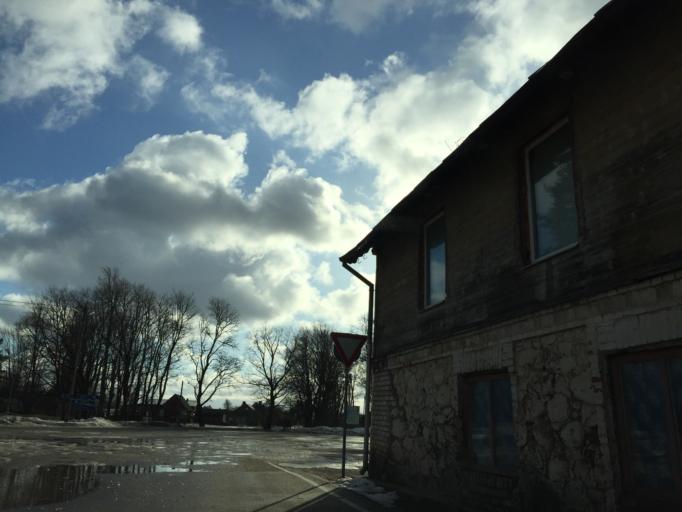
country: LV
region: Limbazu Rajons
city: Limbazi
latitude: 57.6091
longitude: 24.6076
